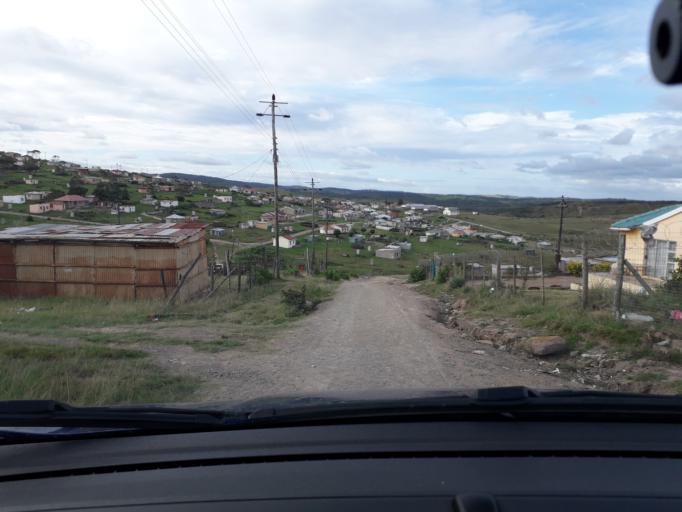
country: ZA
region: Eastern Cape
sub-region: Buffalo City Metropolitan Municipality
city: East London
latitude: -32.8502
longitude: 27.9855
